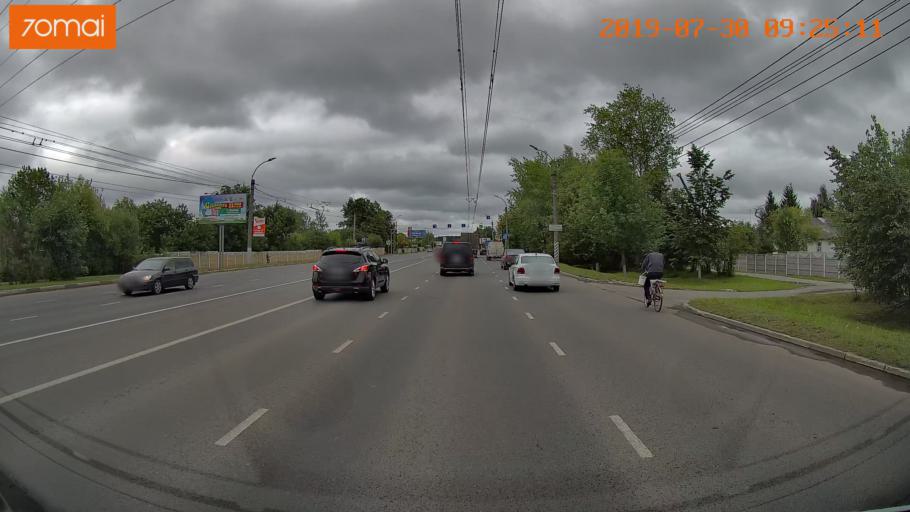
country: RU
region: Ivanovo
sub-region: Gorod Ivanovo
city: Ivanovo
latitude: 56.9538
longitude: 40.9746
